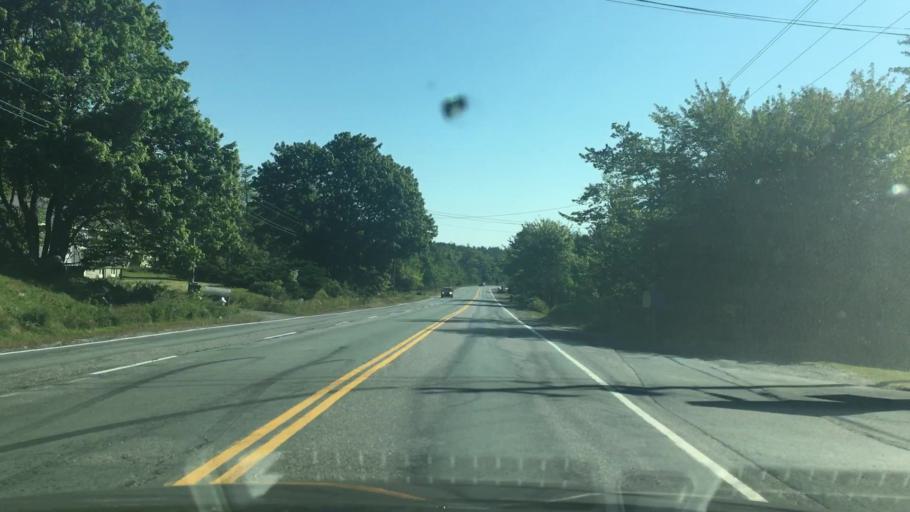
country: CA
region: Nova Scotia
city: Cole Harbour
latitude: 44.7787
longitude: -63.0845
